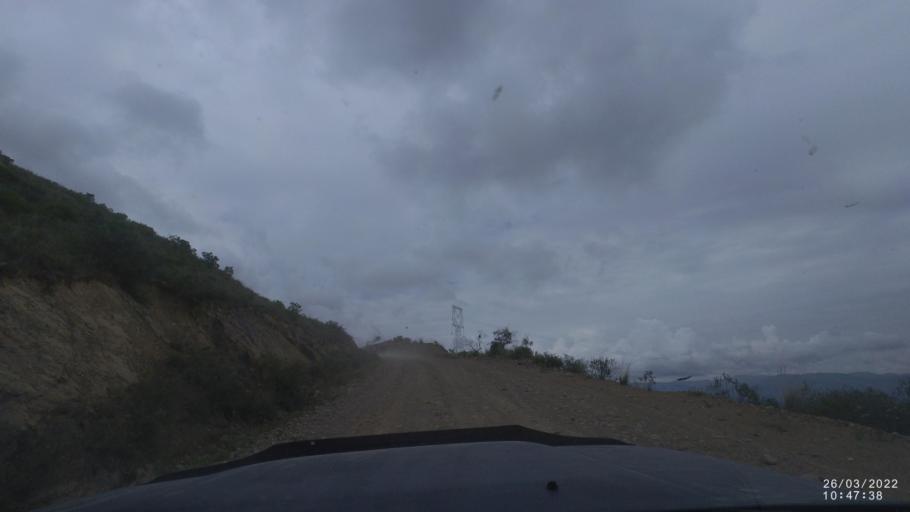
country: BO
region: Cochabamba
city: Tarata
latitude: -17.4930
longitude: -66.0489
